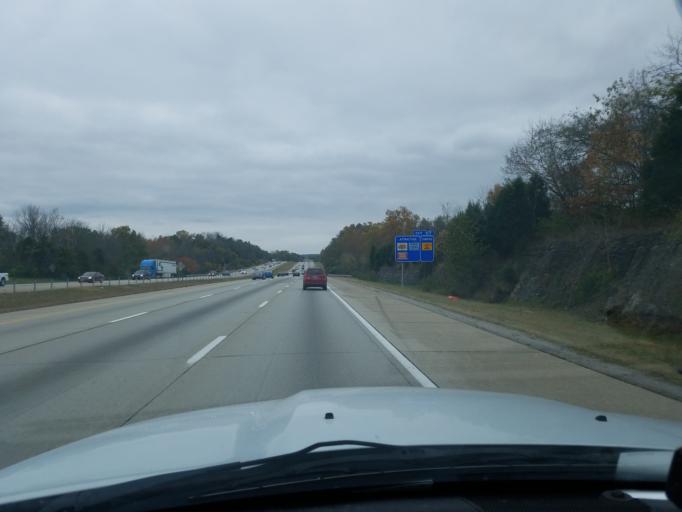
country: US
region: Kentucky
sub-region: Bullitt County
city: Shepherdsville
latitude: 38.0204
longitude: -85.6968
